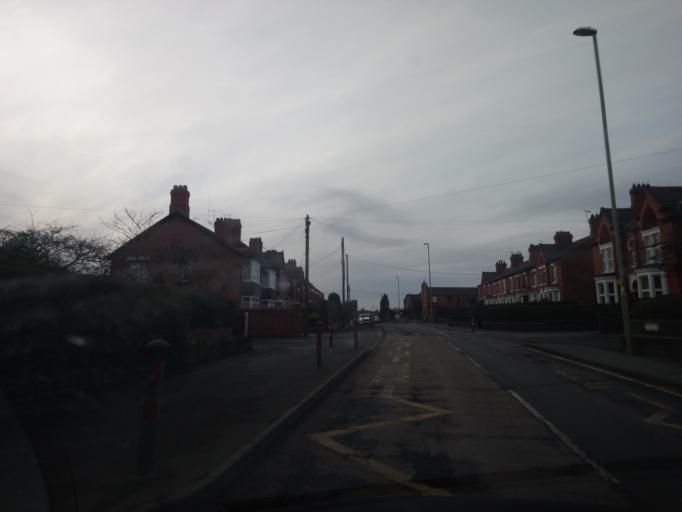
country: GB
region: England
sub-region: Shropshire
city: Whitchurch
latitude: 52.9680
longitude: -2.6743
